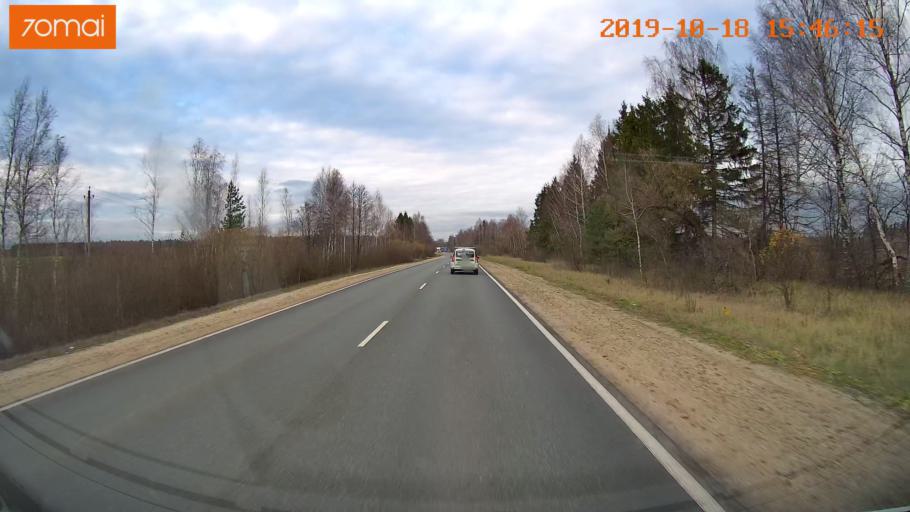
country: RU
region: Vladimir
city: Golovino
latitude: 56.0049
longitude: 40.5684
